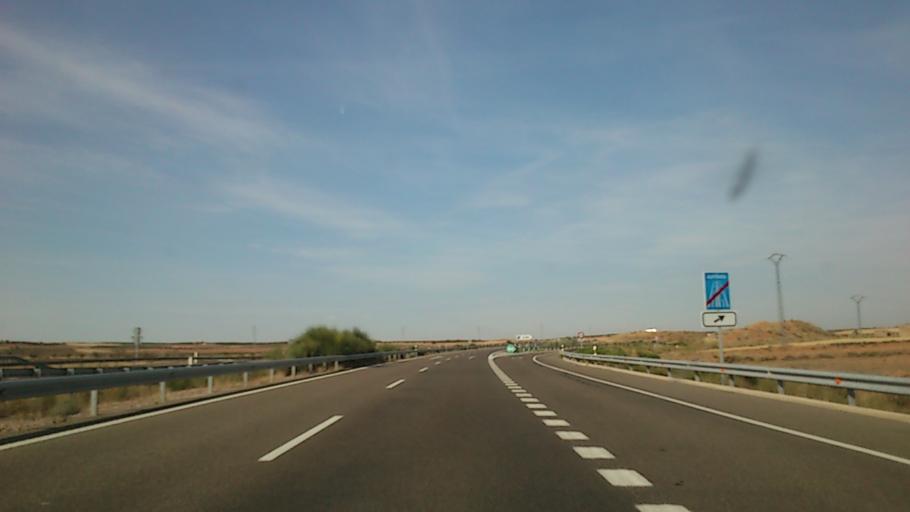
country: ES
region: Aragon
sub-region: Provincia de Zaragoza
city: Longares
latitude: 41.4051
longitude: -1.1772
